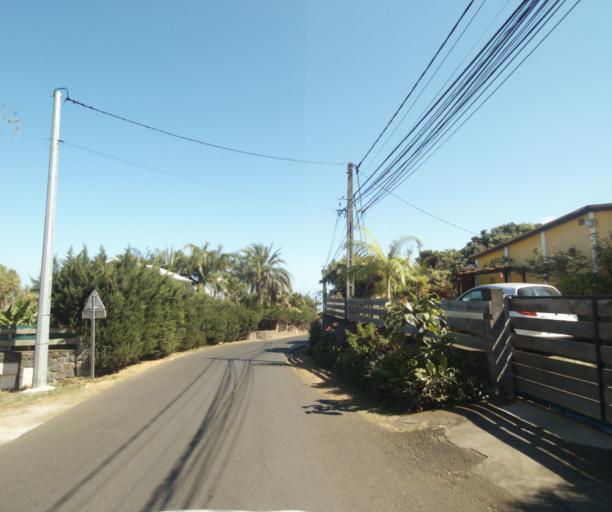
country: RE
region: Reunion
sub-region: Reunion
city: Saint-Paul
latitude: -20.9939
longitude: 55.3263
